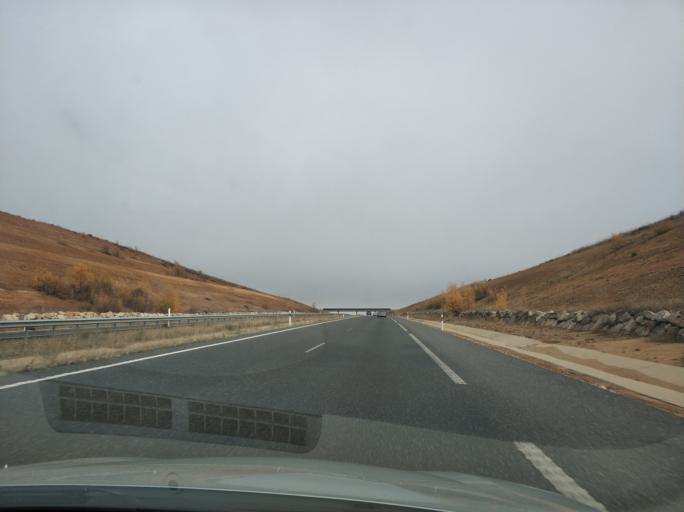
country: ES
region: Castille and Leon
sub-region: Provincia de Leon
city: Valdefresno
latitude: 42.5633
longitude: -5.5291
